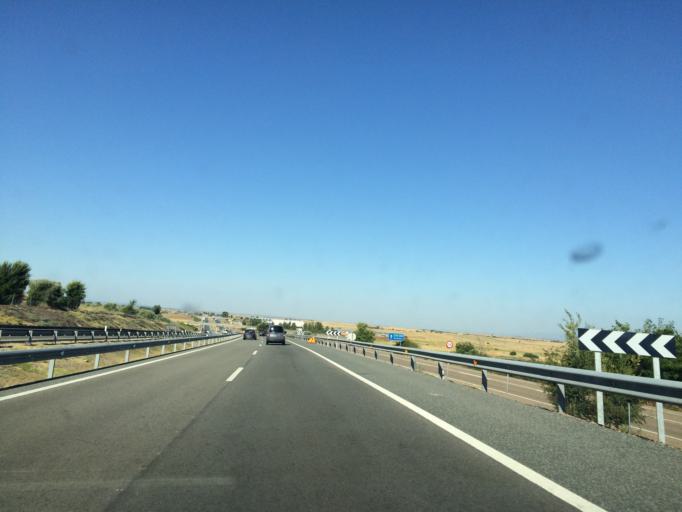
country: ES
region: Castille-La Mancha
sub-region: Province of Toledo
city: Torralba de Oropesa
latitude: 39.9313
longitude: -5.1565
